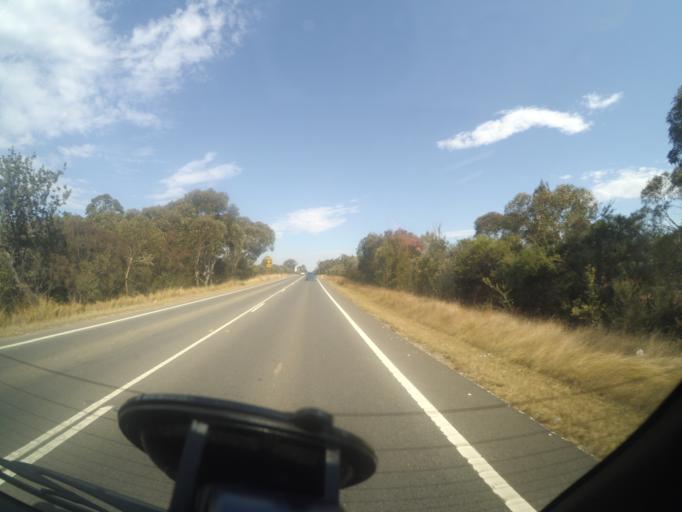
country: AU
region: New South Wales
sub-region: Sutherland Shire
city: Menai
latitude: -34.0095
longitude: 150.9882
